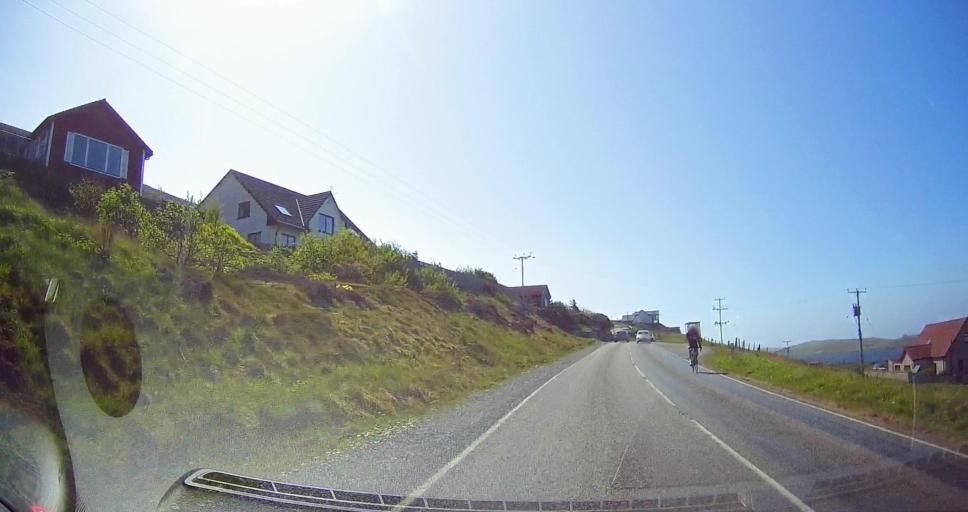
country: GB
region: Scotland
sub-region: Shetland Islands
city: Lerwick
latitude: 60.1324
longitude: -1.2673
